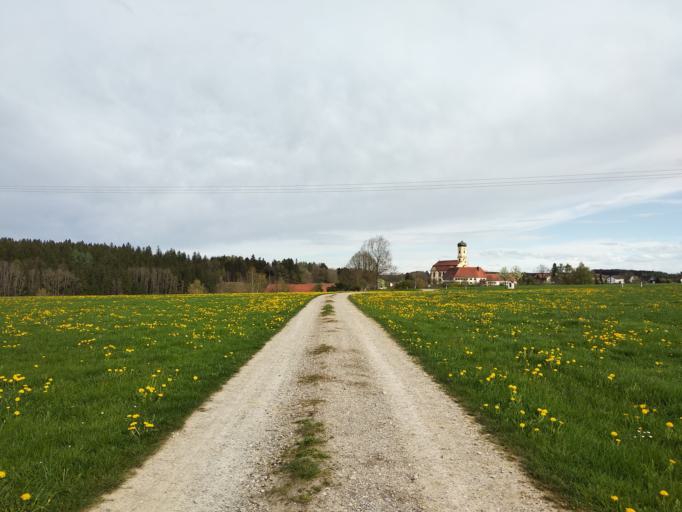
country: DE
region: Bavaria
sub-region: Swabia
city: Lautrach
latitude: 47.8921
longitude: 10.1309
